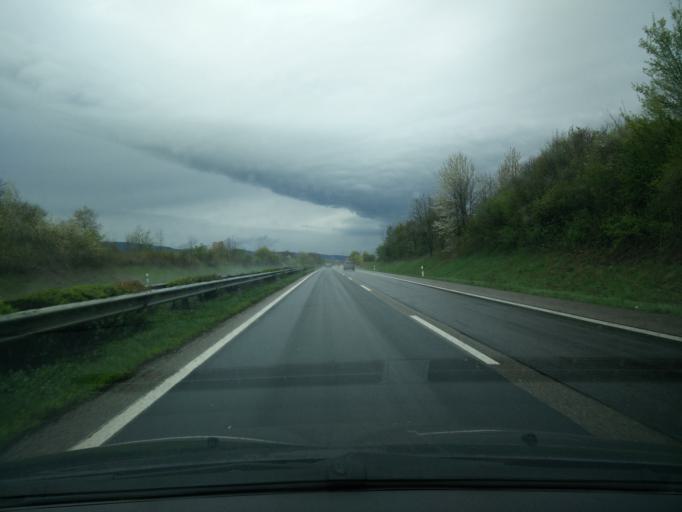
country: DE
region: Rheinland-Pfalz
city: Knoringen
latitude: 49.2417
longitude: 8.1489
